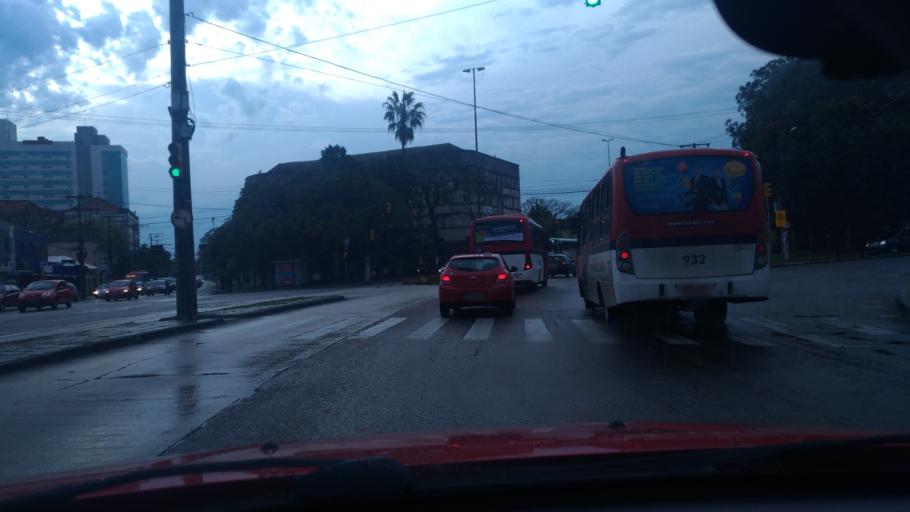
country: BR
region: Rio Grande do Sul
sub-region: Porto Alegre
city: Porto Alegre
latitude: -30.0087
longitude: -51.1793
